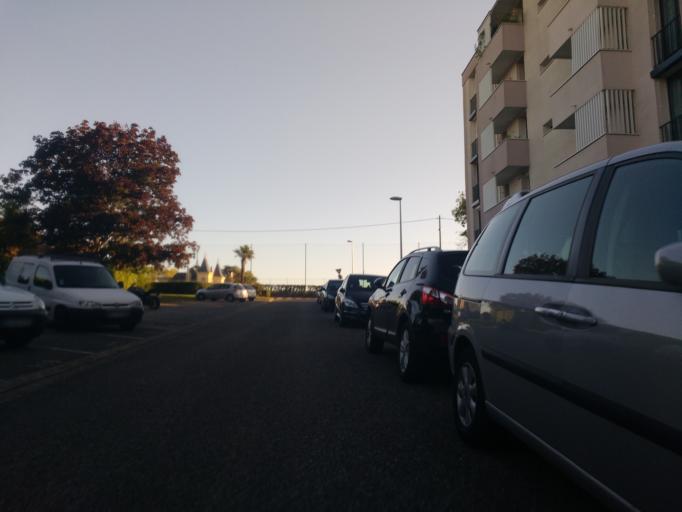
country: FR
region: Aquitaine
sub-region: Departement de la Gironde
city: Pessac
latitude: 44.8139
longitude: -0.6307
